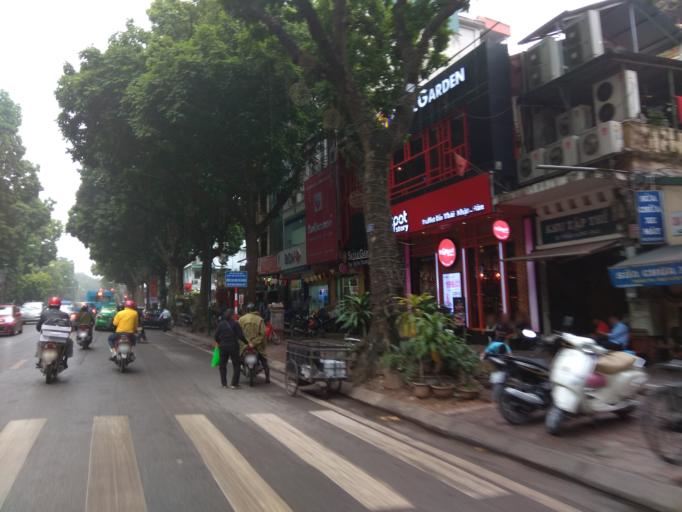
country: VN
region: Ha Noi
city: Hoan Kiem
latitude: 21.0204
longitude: 105.8541
